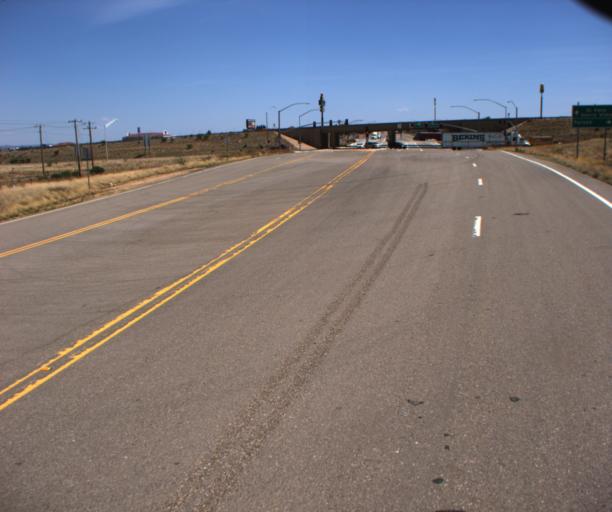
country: US
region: Arizona
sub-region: Cochise County
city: Whetstone
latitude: 31.9665
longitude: -110.3473
